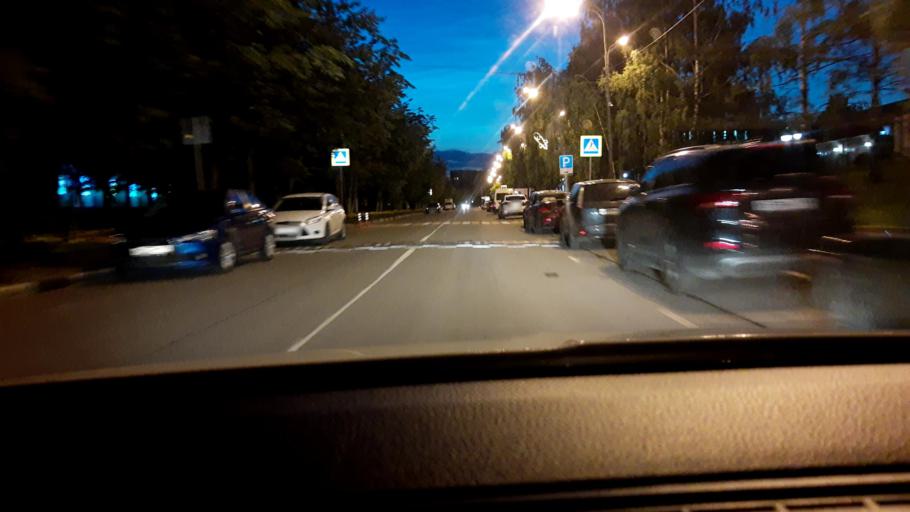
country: RU
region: Moskovskaya
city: Odintsovo
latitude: 55.6757
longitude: 37.2602
